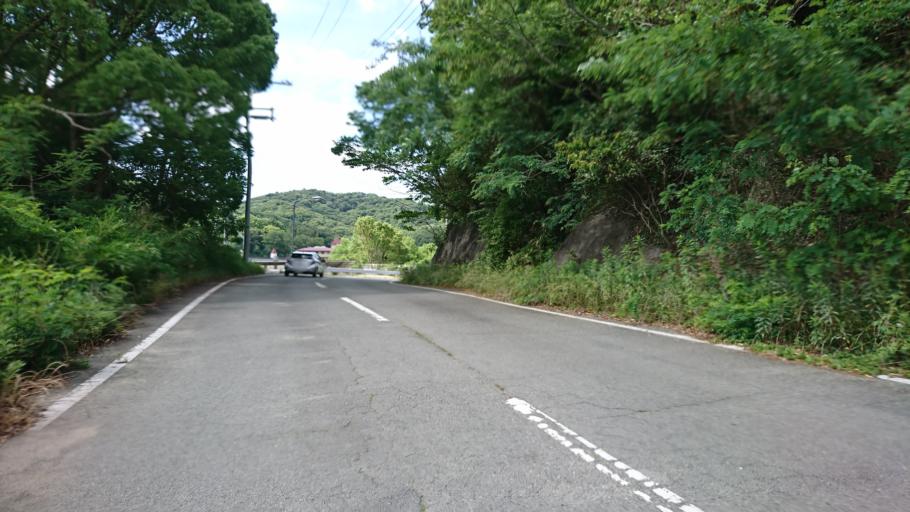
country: JP
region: Hyogo
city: Shirahamacho-usazakiminami
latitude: 34.7952
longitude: 134.7425
